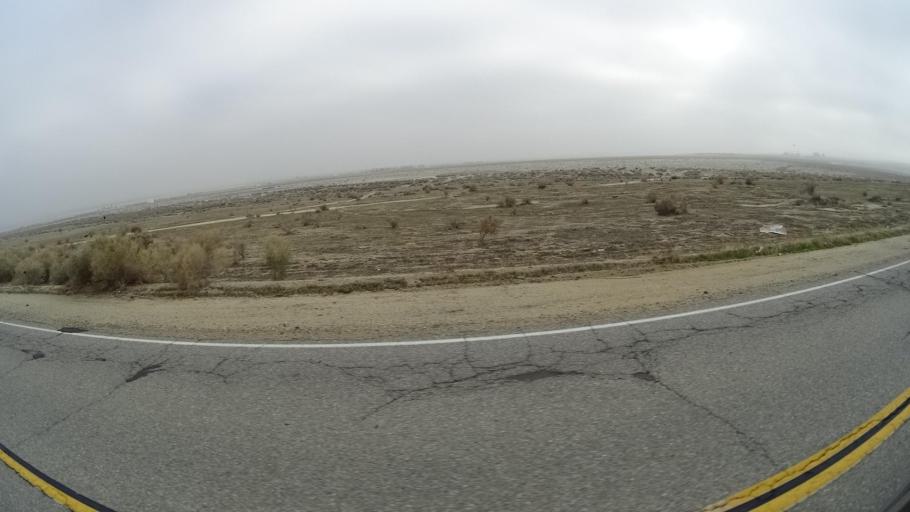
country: US
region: California
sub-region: Kern County
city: South Taft
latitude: 35.1301
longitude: -119.3853
